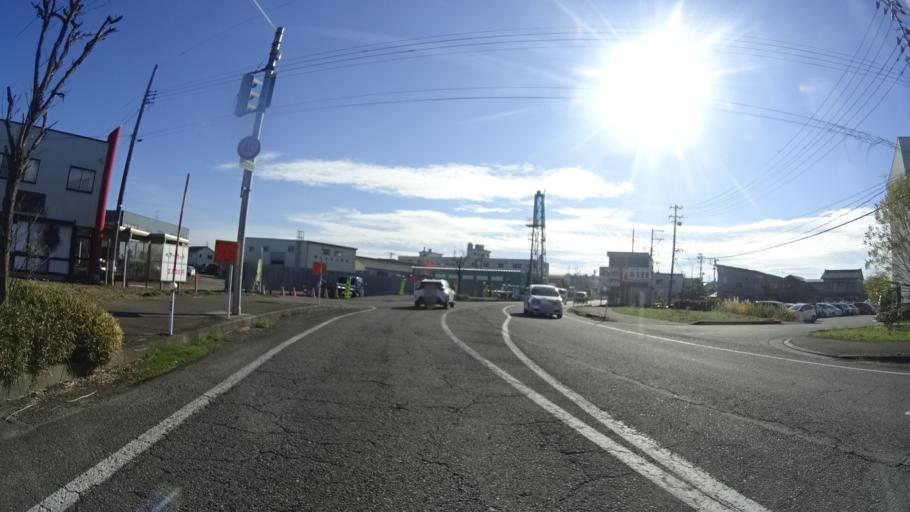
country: JP
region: Niigata
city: Mitsuke
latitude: 37.5407
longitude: 138.9001
